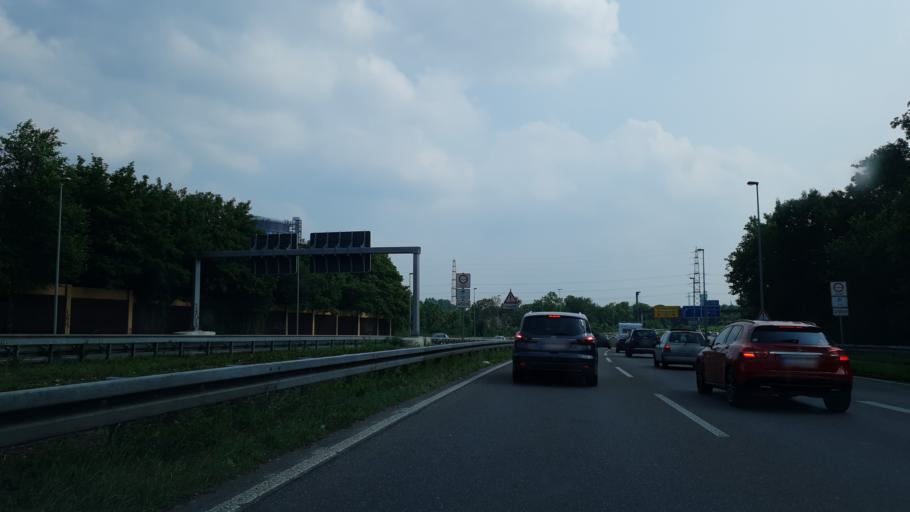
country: DE
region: North Rhine-Westphalia
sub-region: Regierungsbezirk Dusseldorf
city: Oberhausen
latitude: 51.4997
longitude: 6.8644
